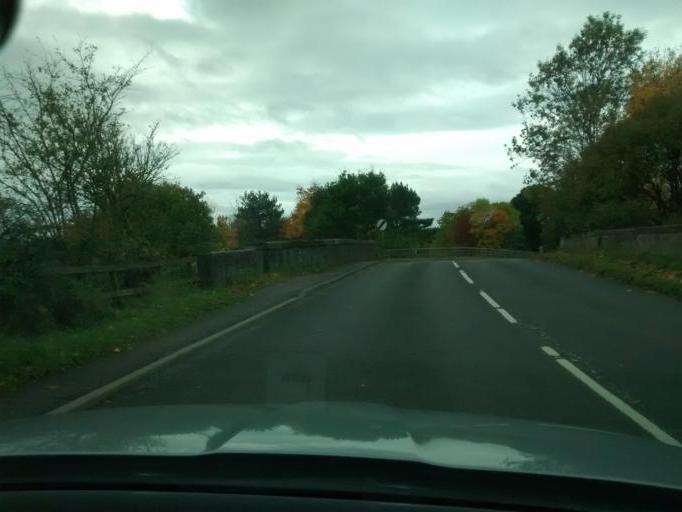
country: GB
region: Scotland
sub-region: Perth and Kinross
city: Luncarty
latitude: 56.4482
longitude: -3.4712
